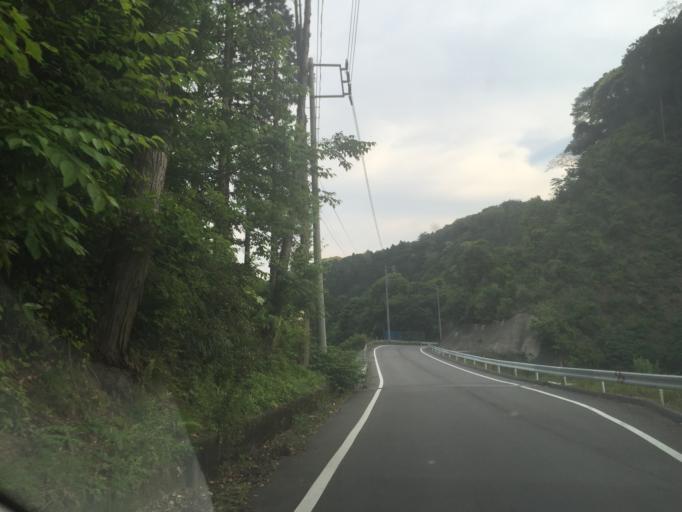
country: JP
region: Shizuoka
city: Kakegawa
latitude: 34.8351
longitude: 138.0148
